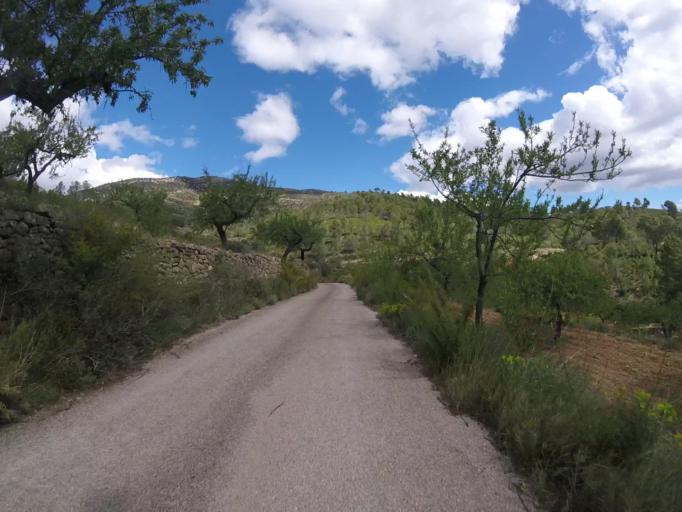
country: ES
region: Valencia
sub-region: Provincia de Castello
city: Sierra-Engarceran
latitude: 40.2815
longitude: -0.0756
